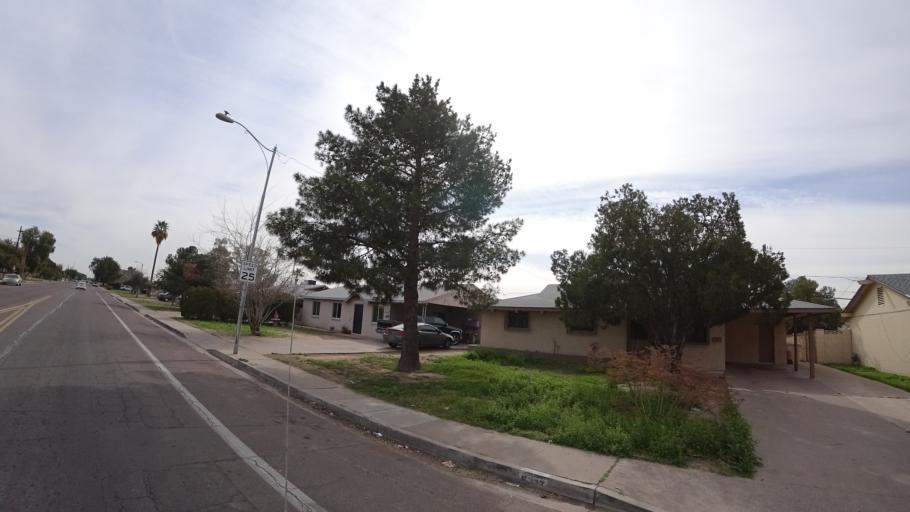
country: US
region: Arizona
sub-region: Maricopa County
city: Glendale
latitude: 33.5312
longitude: -112.1943
